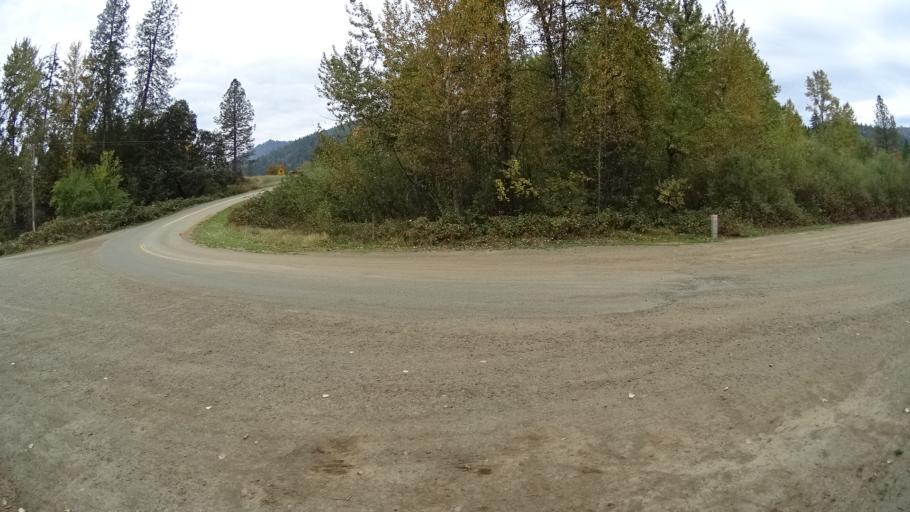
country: US
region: California
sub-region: Siskiyou County
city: Happy Camp
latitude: 41.7954
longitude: -123.3707
